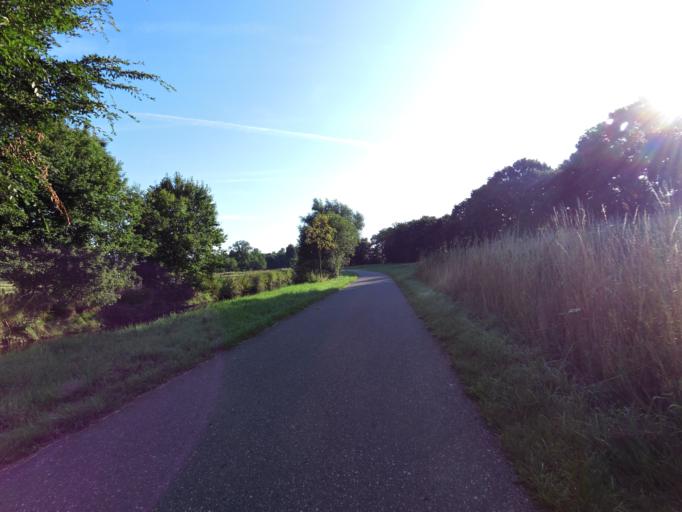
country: DE
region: North Rhine-Westphalia
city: Geilenkirchen
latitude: 50.9931
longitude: 6.1698
